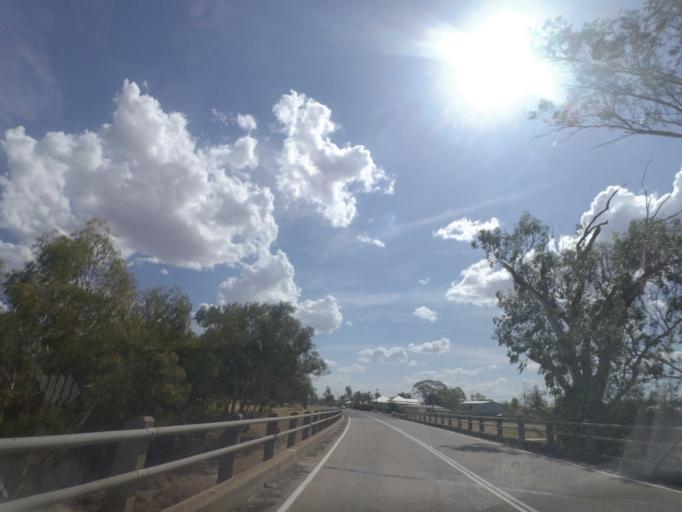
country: AU
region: New South Wales
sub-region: Moree Plains
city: Boggabilla
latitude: -28.4121
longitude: 151.0864
